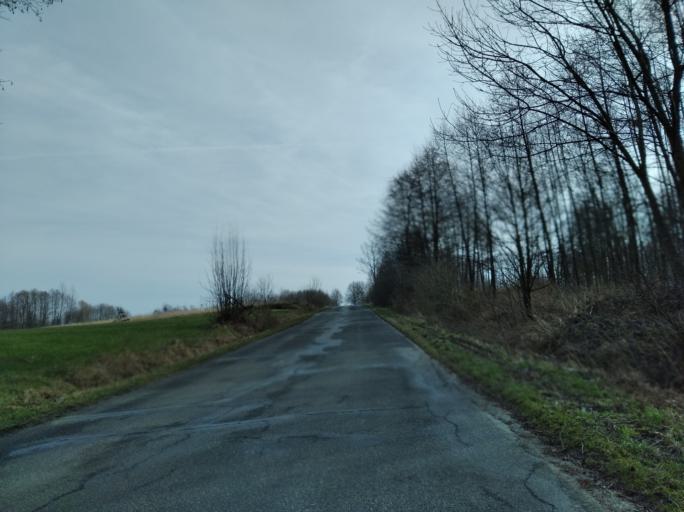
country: PL
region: Subcarpathian Voivodeship
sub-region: Powiat brzozowski
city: Stara Wies
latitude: 49.7143
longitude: 21.9838
